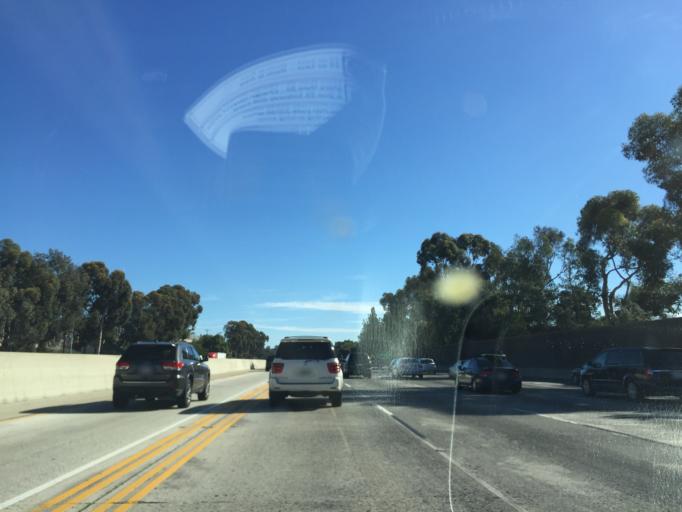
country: US
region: California
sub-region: Orange County
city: Mission Viejo
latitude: 33.6016
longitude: -117.6852
